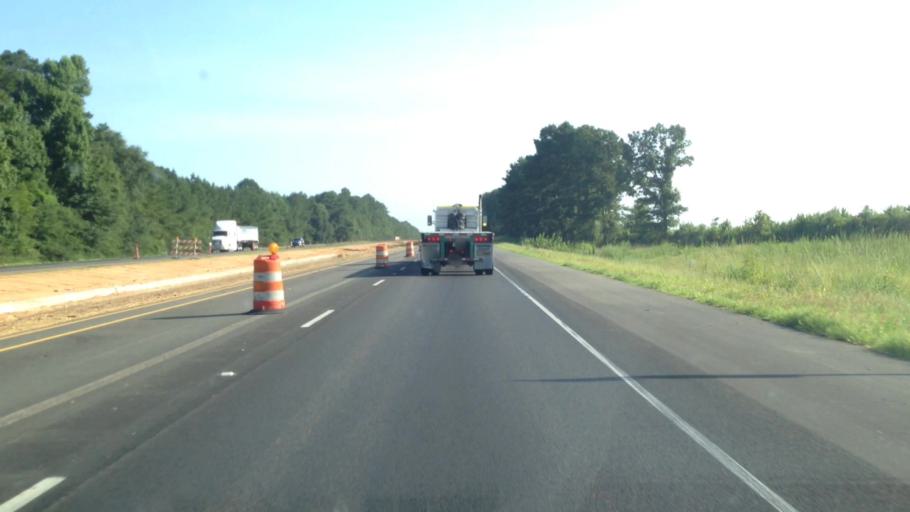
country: US
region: Mississippi
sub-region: Pike County
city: McComb
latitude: 31.1958
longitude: -90.4841
